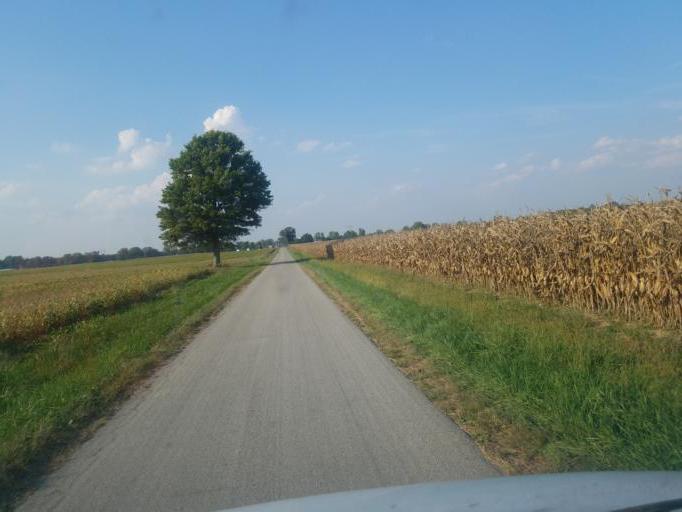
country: US
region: Ohio
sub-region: Wyandot County
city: Upper Sandusky
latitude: 40.9237
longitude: -83.1893
